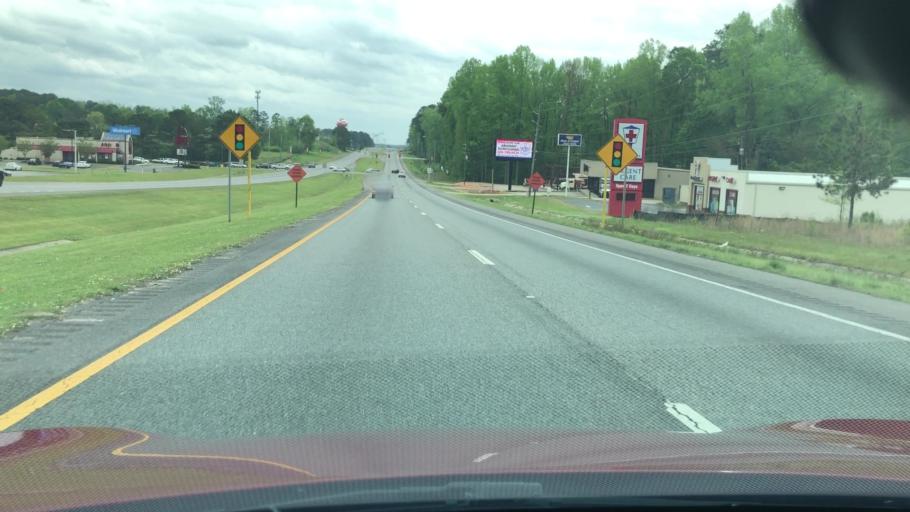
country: US
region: Alabama
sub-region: Tallapoosa County
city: Alexander City
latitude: 32.9403
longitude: -85.9794
